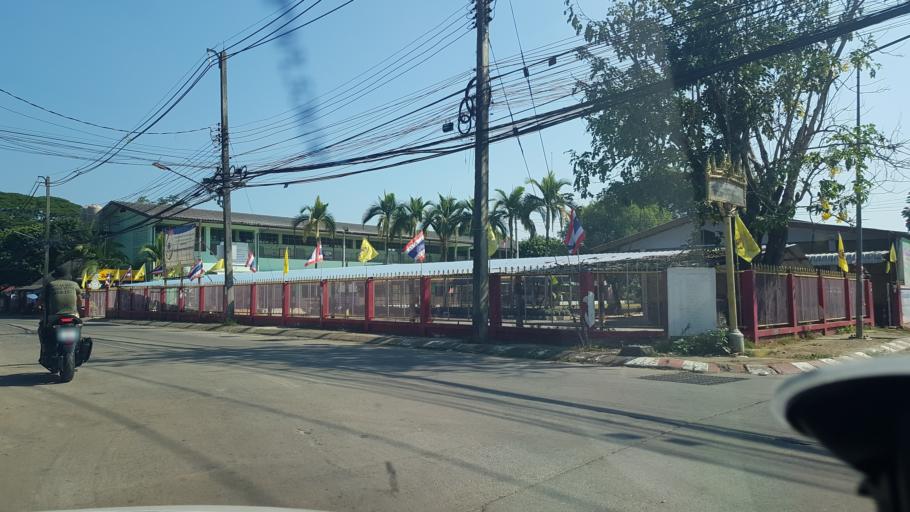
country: TH
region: Chiang Rai
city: Chiang Rai
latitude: 19.9070
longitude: 99.8038
